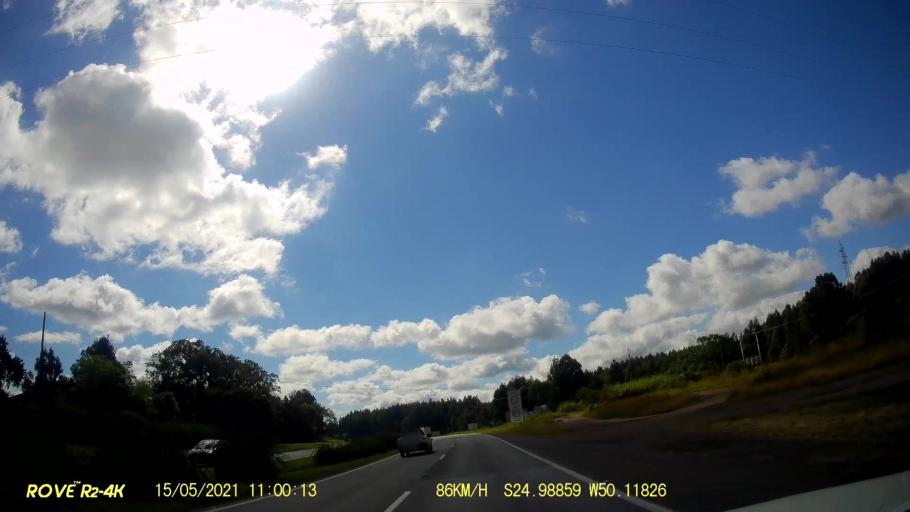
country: BR
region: Parana
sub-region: Carambei
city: Carambei
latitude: -24.9886
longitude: -50.1185
